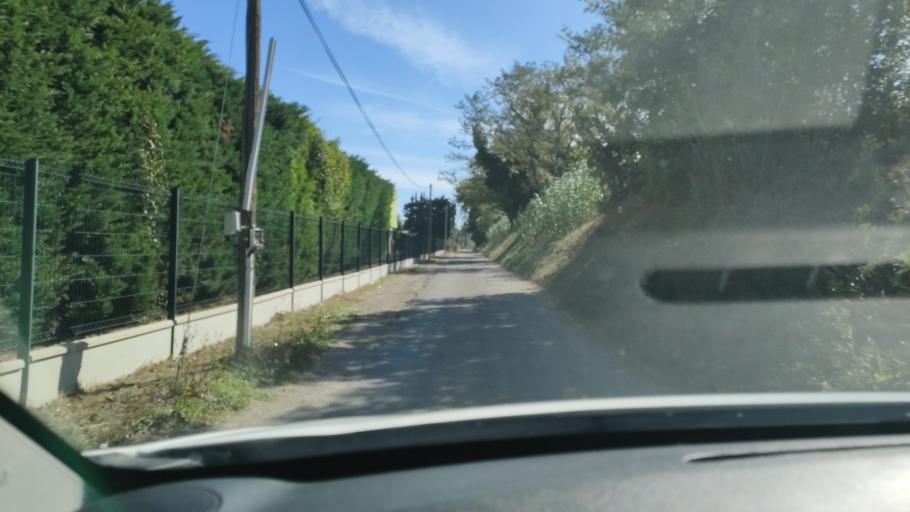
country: FR
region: Provence-Alpes-Cote d'Azur
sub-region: Departement du Vaucluse
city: Morieres-les-Avignon
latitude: 43.9522
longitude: 4.8850
